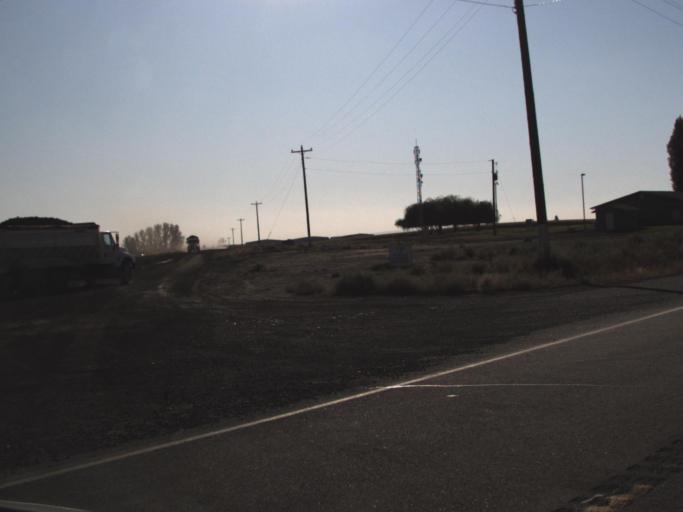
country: US
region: Washington
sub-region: Walla Walla County
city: Garrett
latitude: 46.2965
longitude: -118.6367
